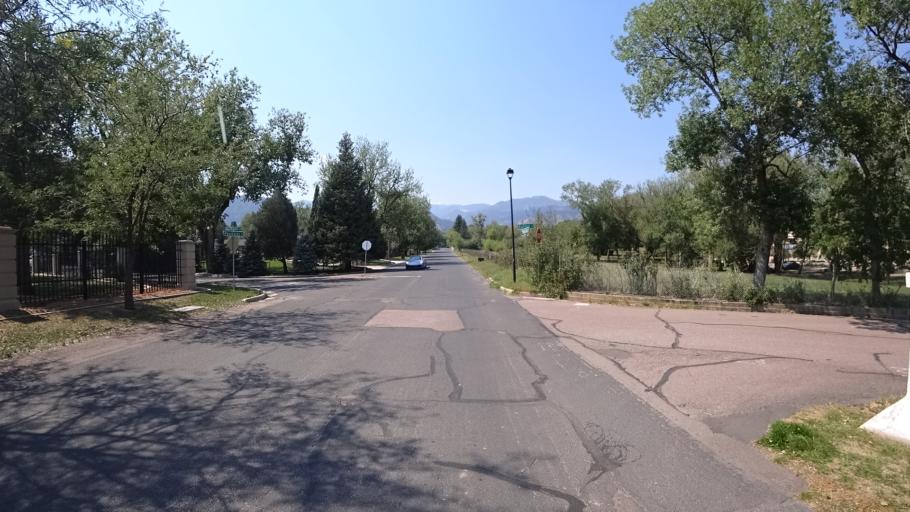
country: US
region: Colorado
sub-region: El Paso County
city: Colorado Springs
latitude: 38.7885
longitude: -104.8398
